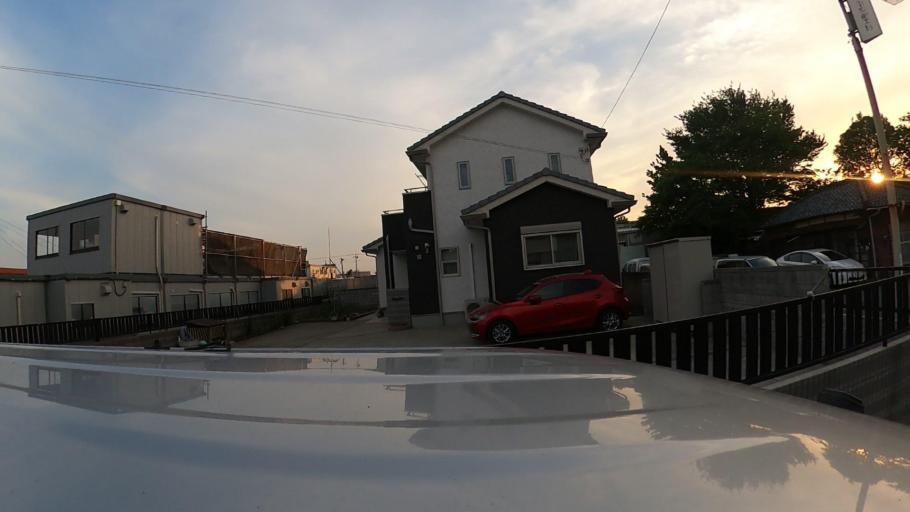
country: JP
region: Ibaraki
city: Ushiku
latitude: 36.0284
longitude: 140.0898
